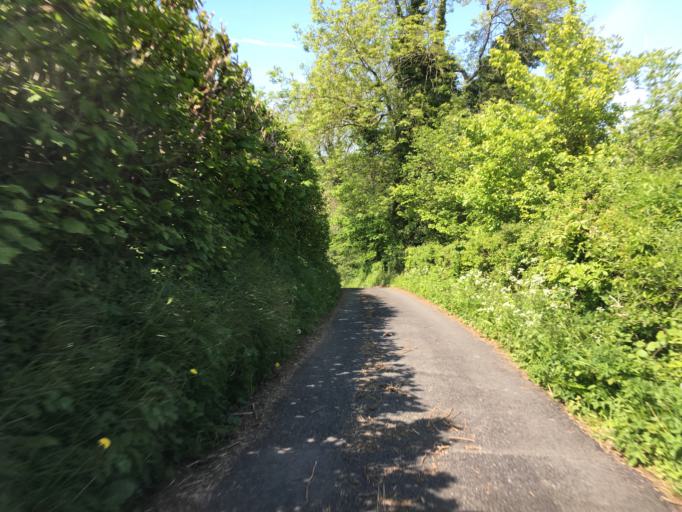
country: GB
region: England
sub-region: Gloucestershire
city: Brimscombe
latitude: 51.7229
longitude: -2.2043
